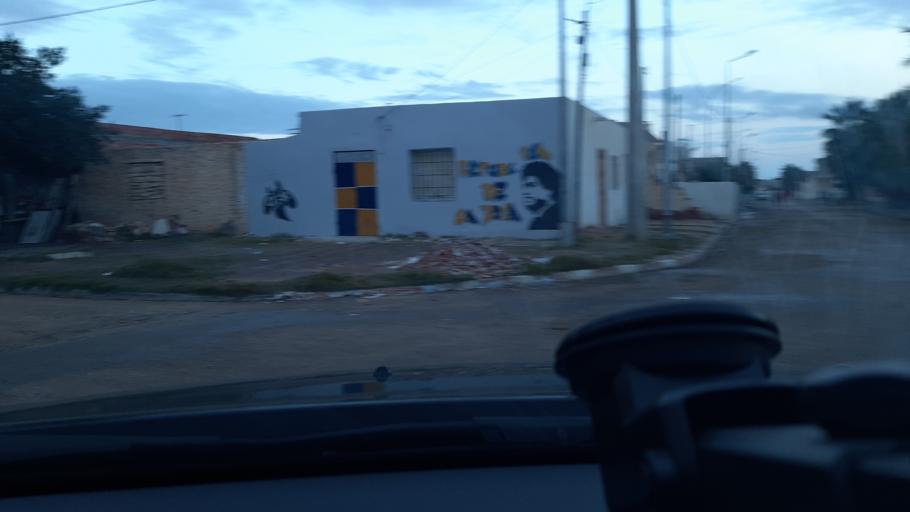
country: TN
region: Al Mahdiyah
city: Shurban
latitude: 34.9660
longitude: 10.3694
